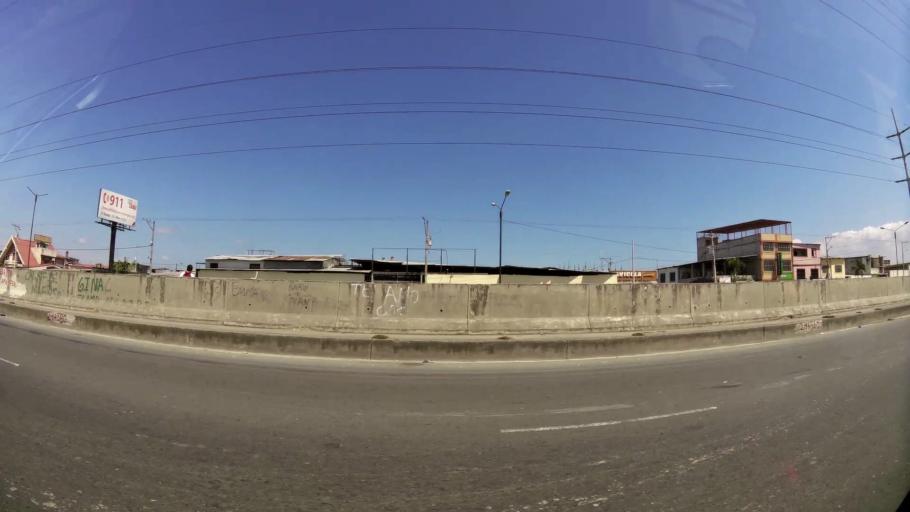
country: EC
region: Guayas
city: Guayaquil
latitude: -2.2374
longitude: -79.9281
